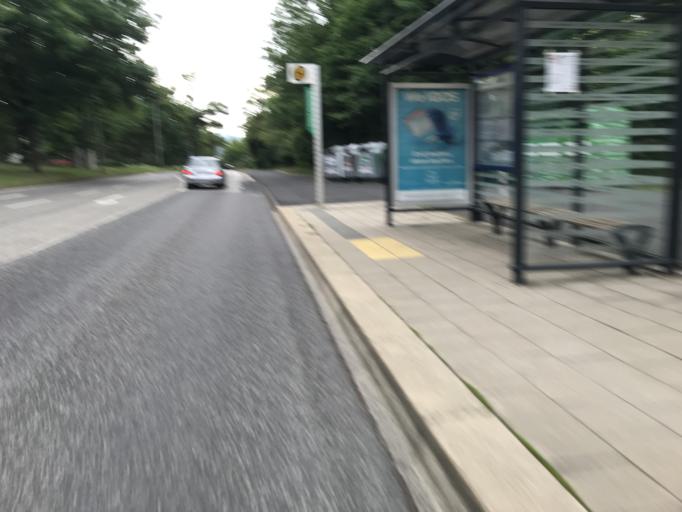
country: DE
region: Hesse
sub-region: Regierungsbezirk Kassel
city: Fuldabruck
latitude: 51.2935
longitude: 9.4453
